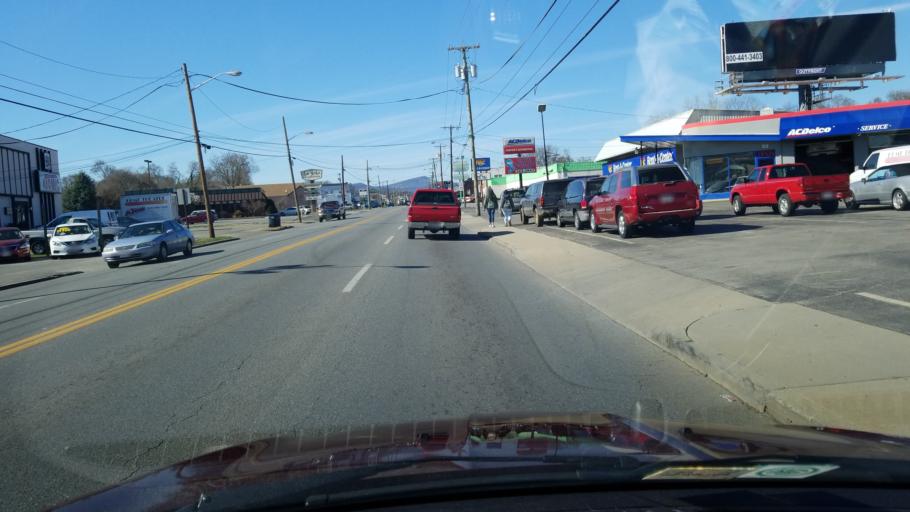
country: US
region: Virginia
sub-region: City of Roanoke
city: Roanoke
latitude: 37.2960
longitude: -79.9371
